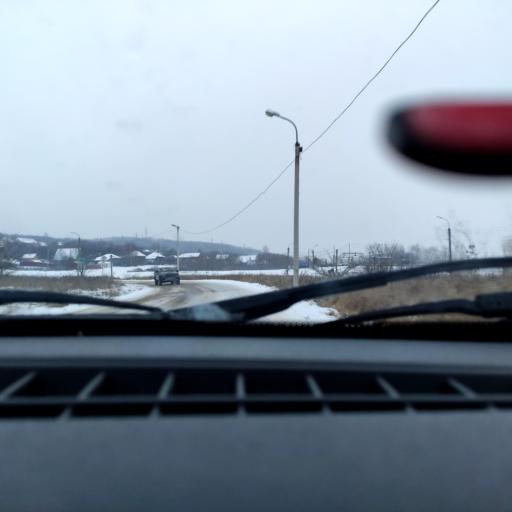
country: RU
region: Bashkortostan
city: Blagoveshchensk
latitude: 54.8896
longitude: 56.0356
